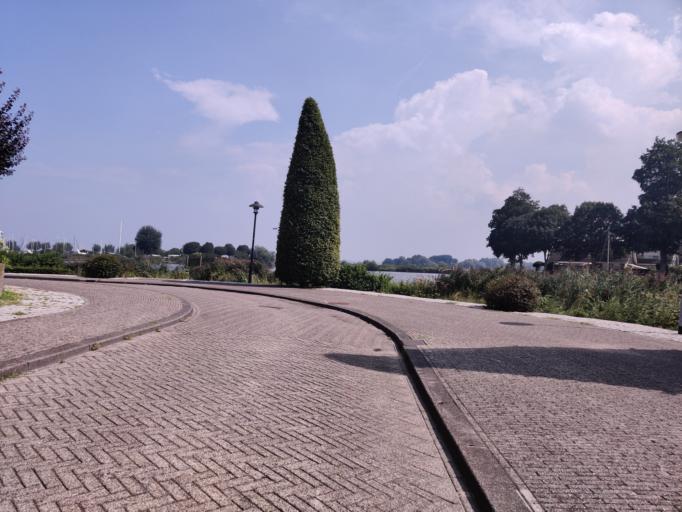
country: NL
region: Flevoland
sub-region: Gemeente Zeewolde
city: Zeewolde
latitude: 52.3314
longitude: 5.5487
